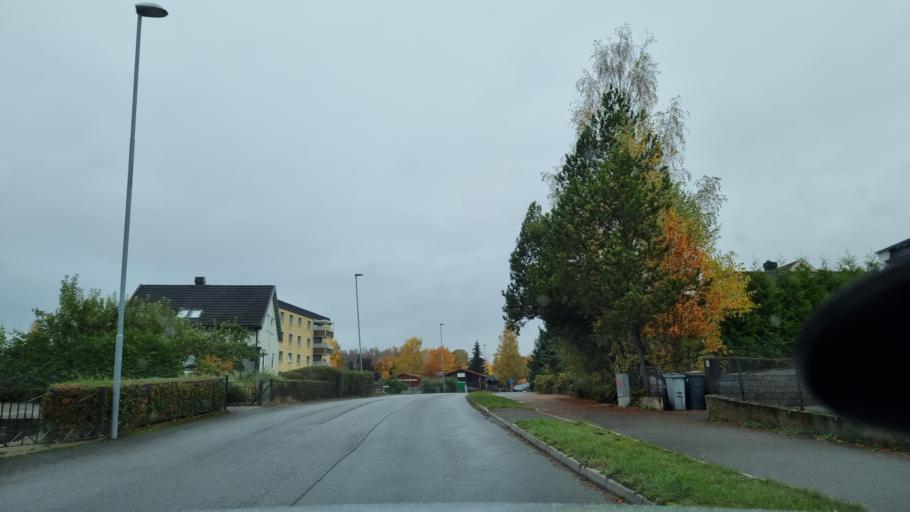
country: NO
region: Hedmark
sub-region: Hamar
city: Hamar
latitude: 60.7980
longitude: 11.0928
